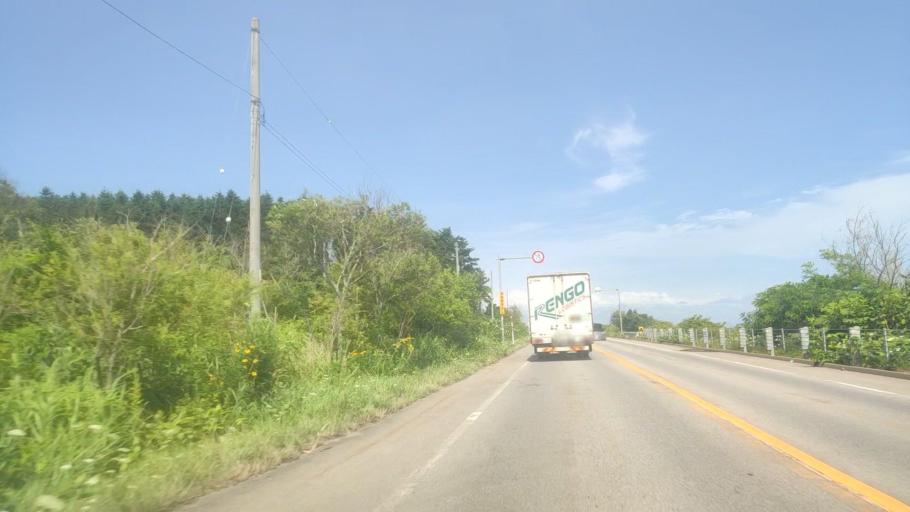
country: JP
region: Hokkaido
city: Nanae
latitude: 42.1821
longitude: 140.4390
